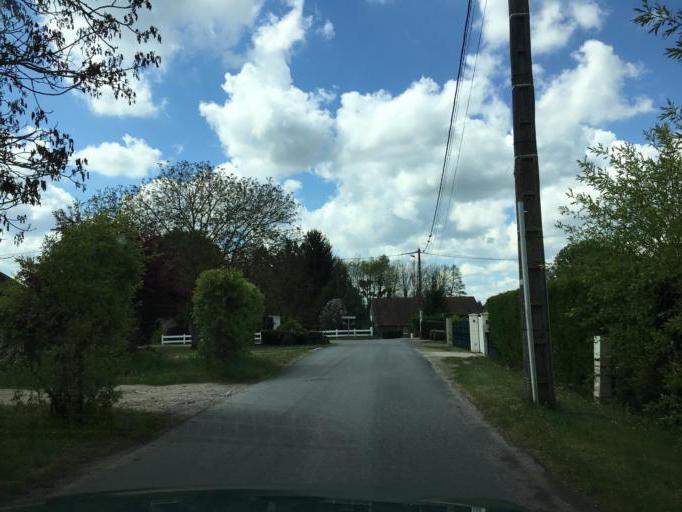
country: FR
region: Centre
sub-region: Departement du Loiret
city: Clery-Saint-Andre
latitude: 47.8222
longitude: 1.7921
